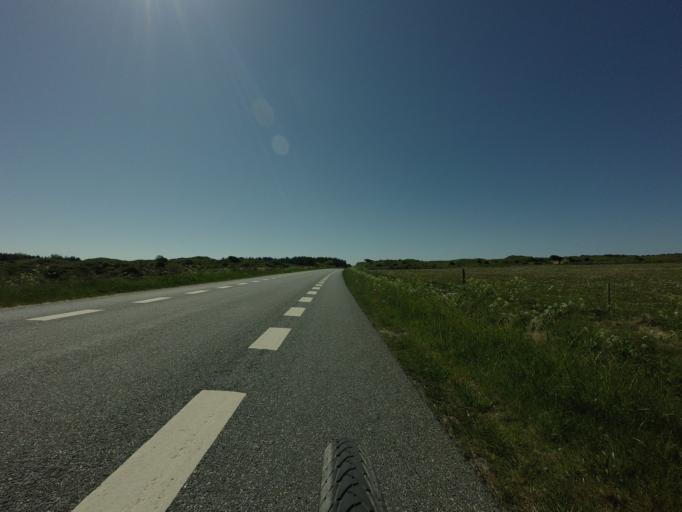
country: DK
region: North Denmark
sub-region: Hjorring Kommune
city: Hjorring
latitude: 57.4533
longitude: 9.7966
